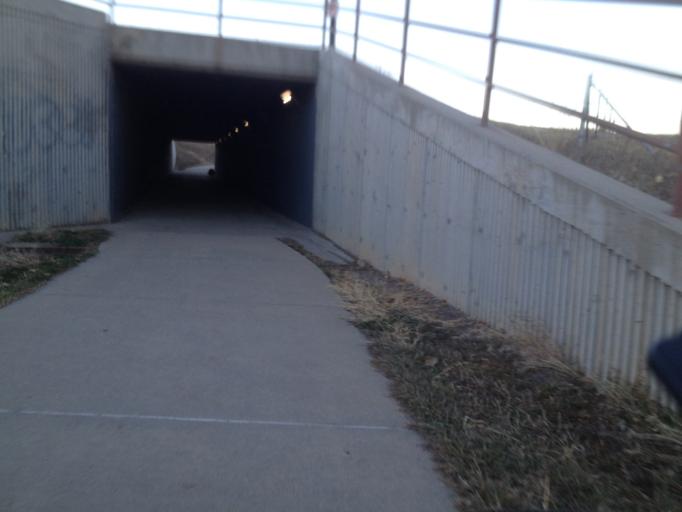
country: US
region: Colorado
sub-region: Boulder County
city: Superior
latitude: 39.9542
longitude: -105.1468
